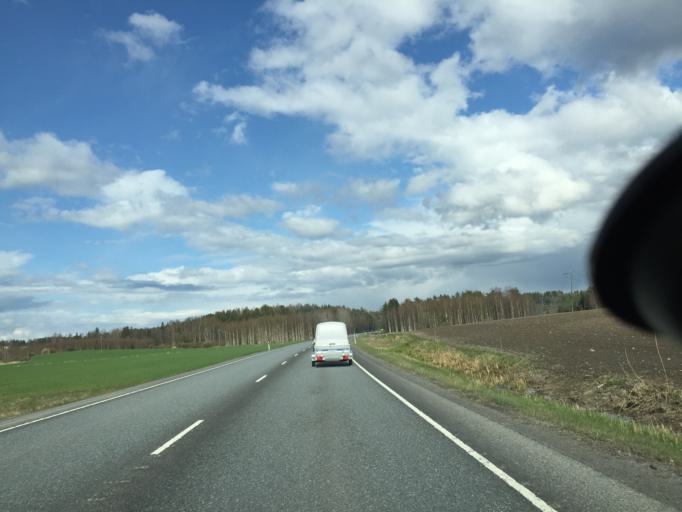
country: FI
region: Uusimaa
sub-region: Raaseporin
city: Karis
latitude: 60.0605
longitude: 23.6717
